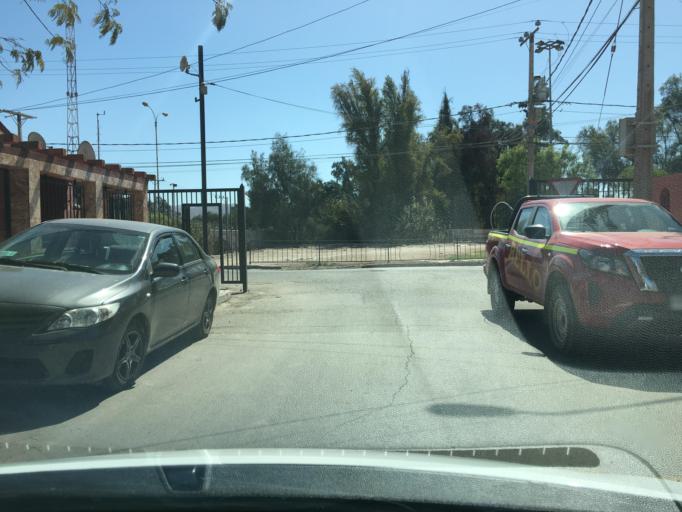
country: CL
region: Atacama
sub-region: Provincia de Copiapo
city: Copiapo
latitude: -27.4112
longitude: -70.2877
